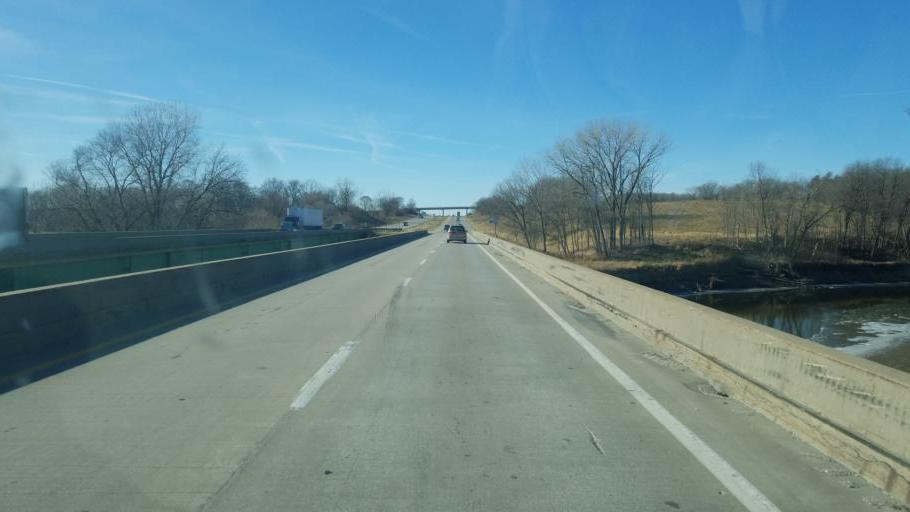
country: US
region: Iowa
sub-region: Dallas County
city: Van Meter
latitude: 41.5454
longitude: -93.9665
